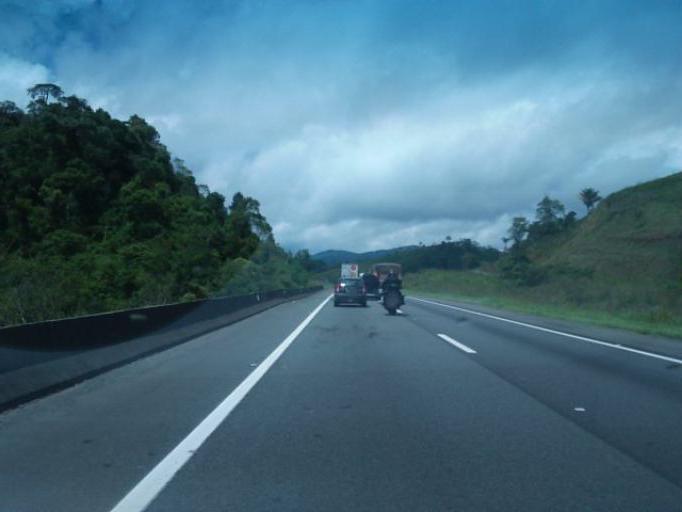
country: BR
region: Parana
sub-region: Antonina
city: Antonina
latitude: -25.0431
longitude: -48.5406
